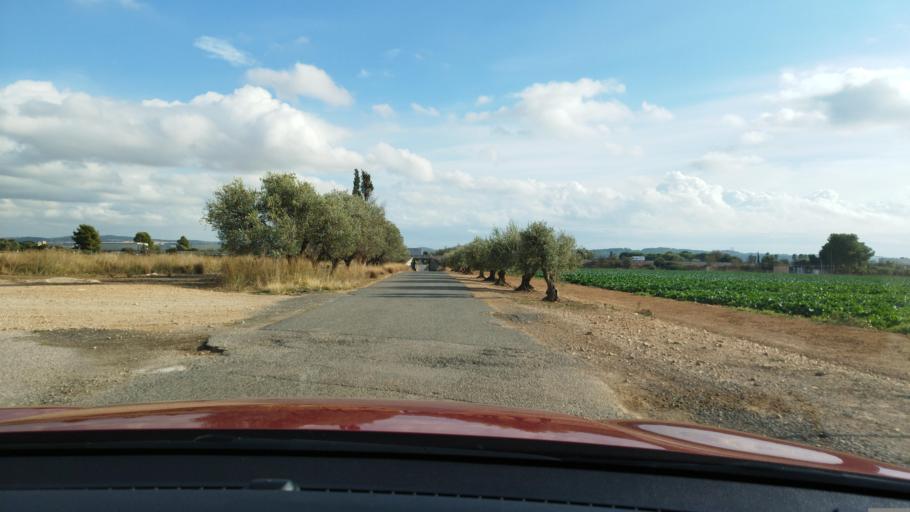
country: ES
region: Catalonia
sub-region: Provincia de Tarragona
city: Santa Oliva
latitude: 41.2546
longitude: 1.5337
